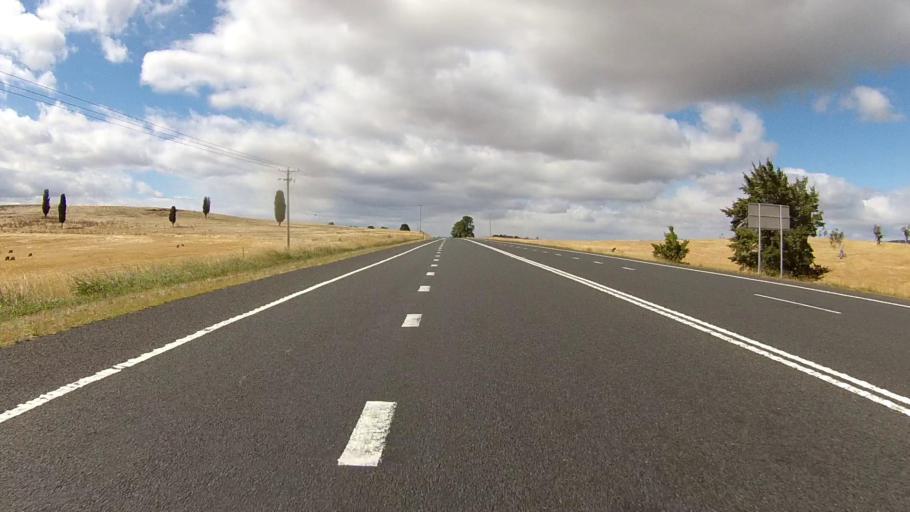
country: AU
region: Tasmania
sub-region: Northern Midlands
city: Evandale
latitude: -41.8767
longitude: 147.4610
